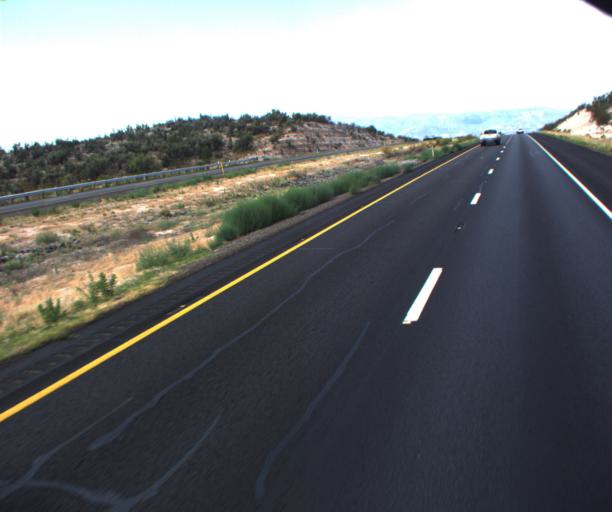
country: US
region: Arizona
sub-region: Yavapai County
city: Camp Verde
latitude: 34.6209
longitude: -111.8442
